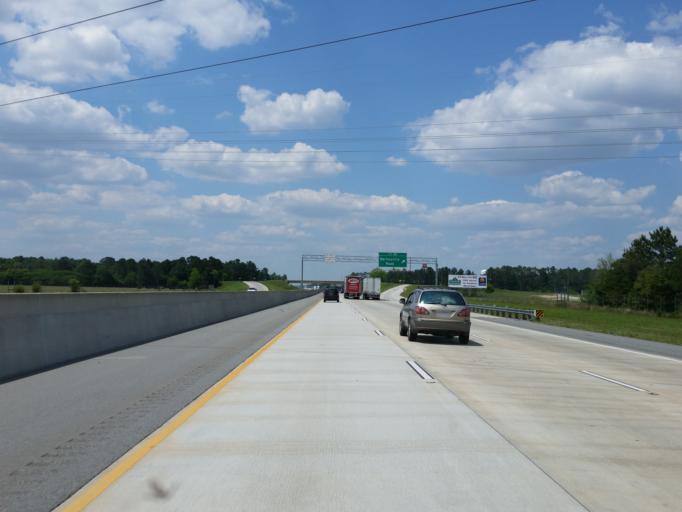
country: US
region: Georgia
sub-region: Cook County
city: Sparks
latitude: 31.2100
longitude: -83.4590
